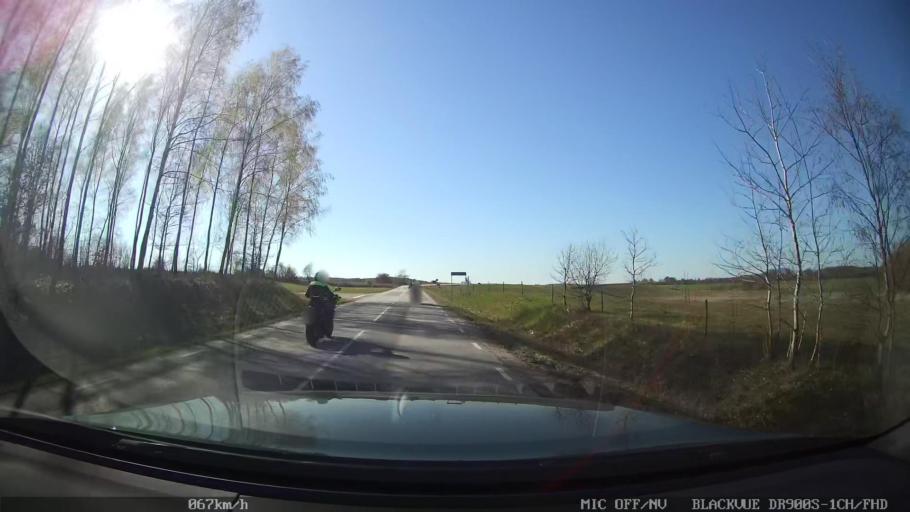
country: SE
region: Skane
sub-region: Klippans Kommun
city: Ljungbyhed
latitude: 55.9692
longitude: 13.2112
